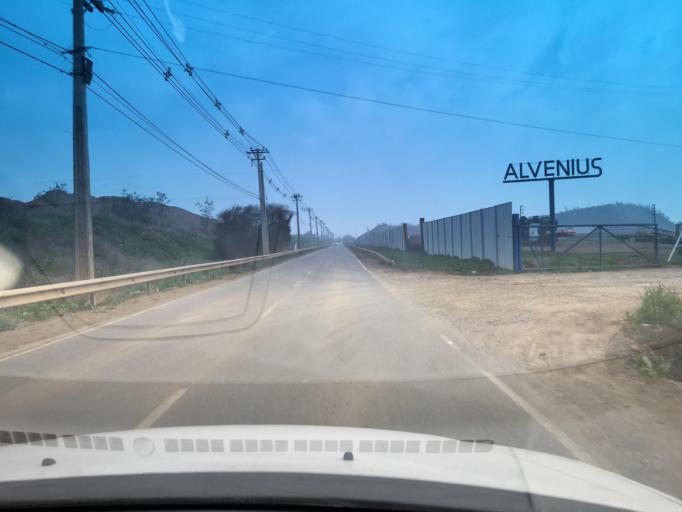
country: CL
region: Santiago Metropolitan
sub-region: Provincia de Chacabuco
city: Lampa
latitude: -33.3620
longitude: -70.8004
